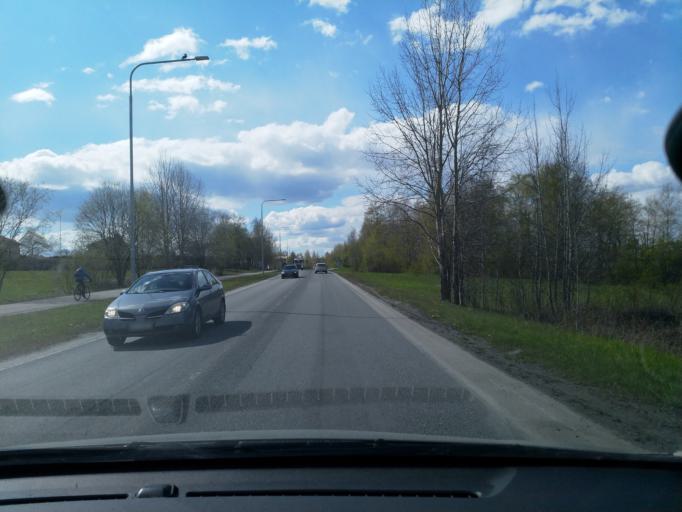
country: FI
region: Pirkanmaa
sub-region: Tampere
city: Tampere
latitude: 61.4798
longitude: 23.8189
